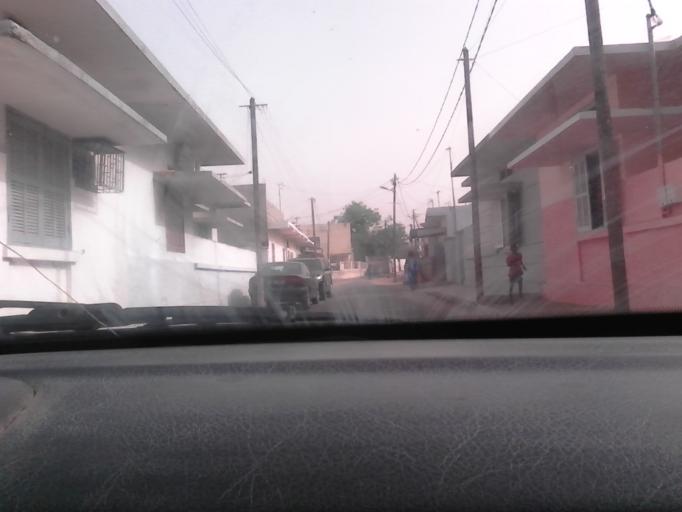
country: SN
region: Dakar
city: Grand Dakar
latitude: 14.7033
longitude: -17.4532
